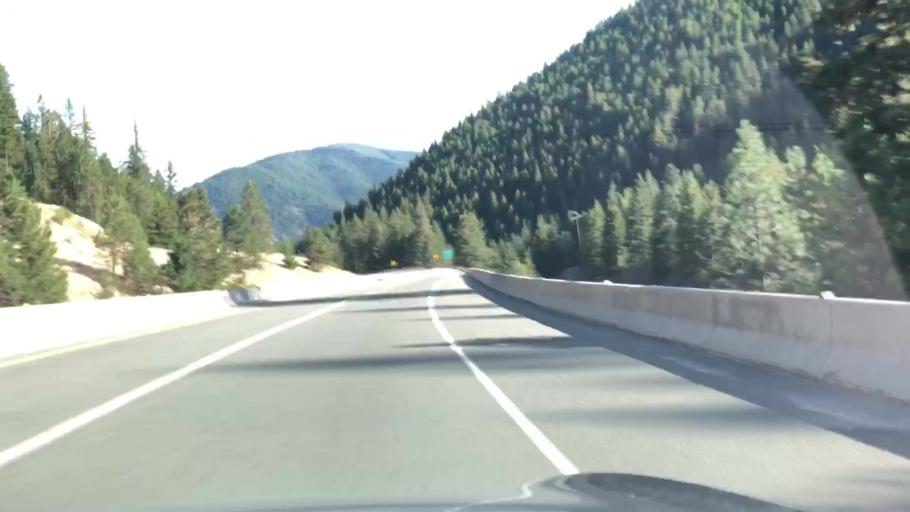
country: US
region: Montana
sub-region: Sanders County
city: Thompson Falls
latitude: 47.3300
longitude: -115.2587
